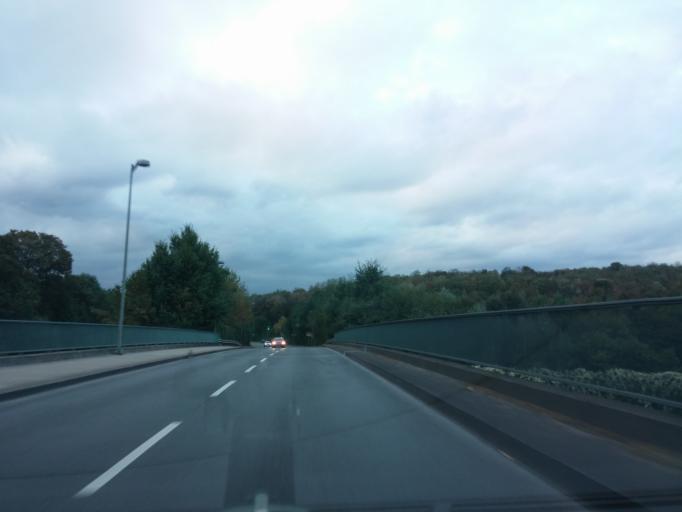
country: DE
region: North Rhine-Westphalia
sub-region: Regierungsbezirk Munster
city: Gladbeck
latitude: 51.5578
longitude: 7.0350
